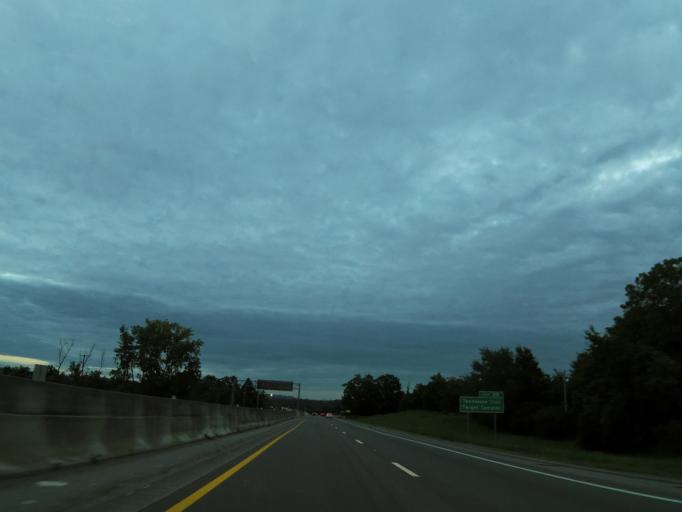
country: US
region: Tennessee
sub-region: Davidson County
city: Nashville
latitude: 36.1811
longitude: -86.8683
